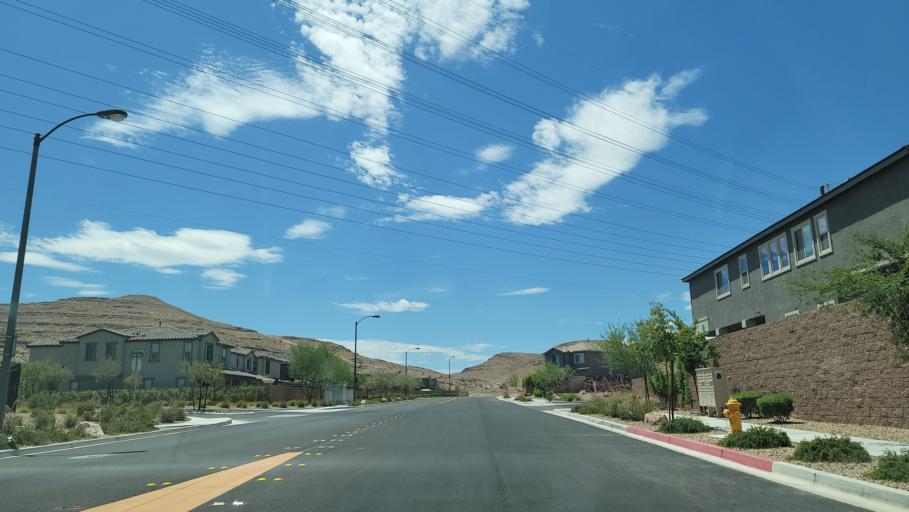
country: US
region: Nevada
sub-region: Clark County
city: Enterprise
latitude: 35.9907
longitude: -115.2346
